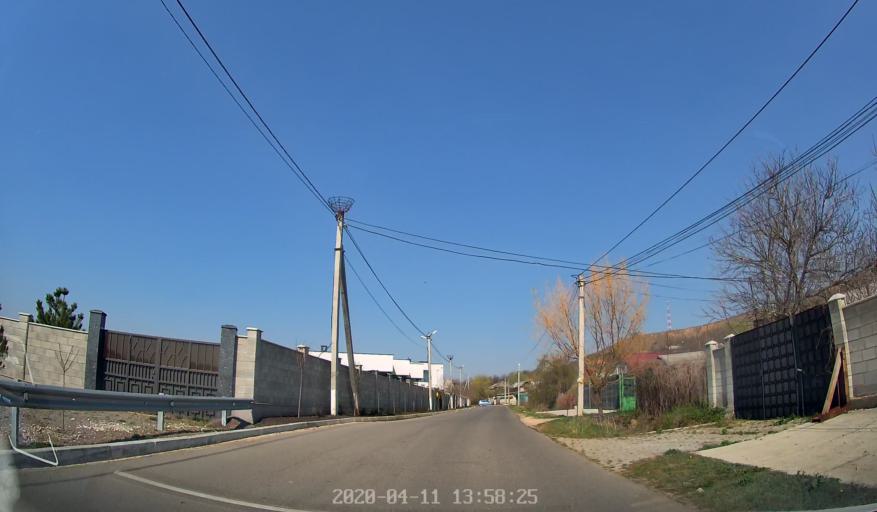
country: MD
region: Chisinau
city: Vadul lui Voda
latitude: 47.0790
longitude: 29.1297
